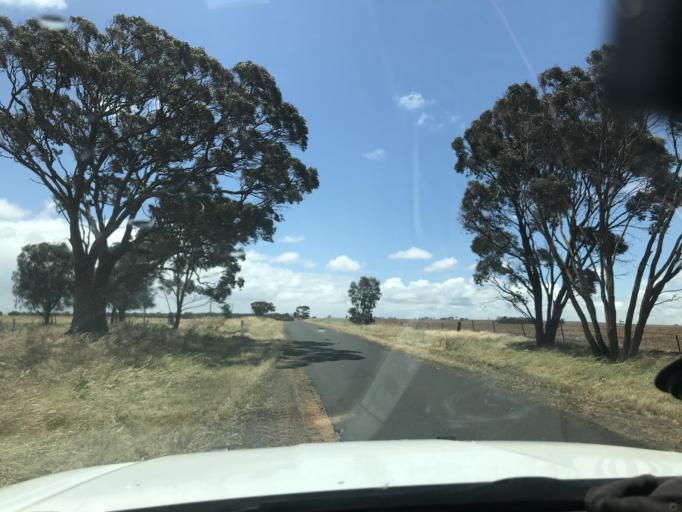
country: AU
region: South Australia
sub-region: Tatiara
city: Bordertown
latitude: -36.4113
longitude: 141.3304
